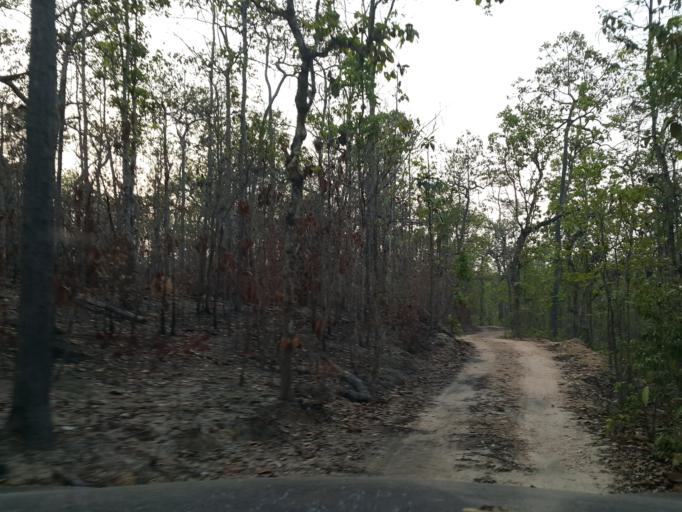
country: TH
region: Lamphun
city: Thung Hua Chang
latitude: 17.9075
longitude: 99.0815
